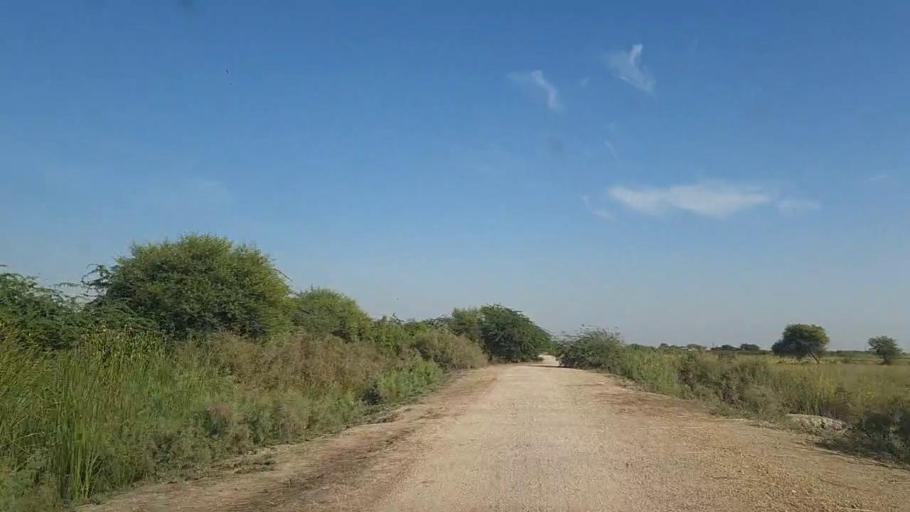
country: PK
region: Sindh
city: Mirpur Batoro
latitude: 24.7624
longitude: 68.3540
